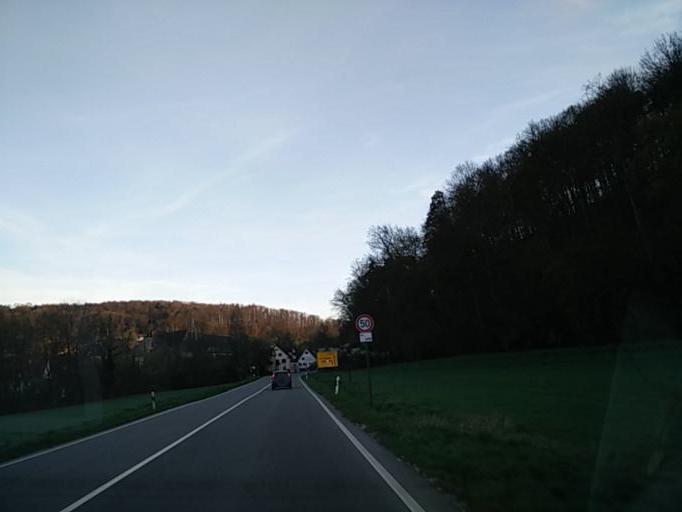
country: DE
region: Baden-Wuerttemberg
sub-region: Tuebingen Region
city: Tuebingen
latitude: 48.5587
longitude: 9.0643
